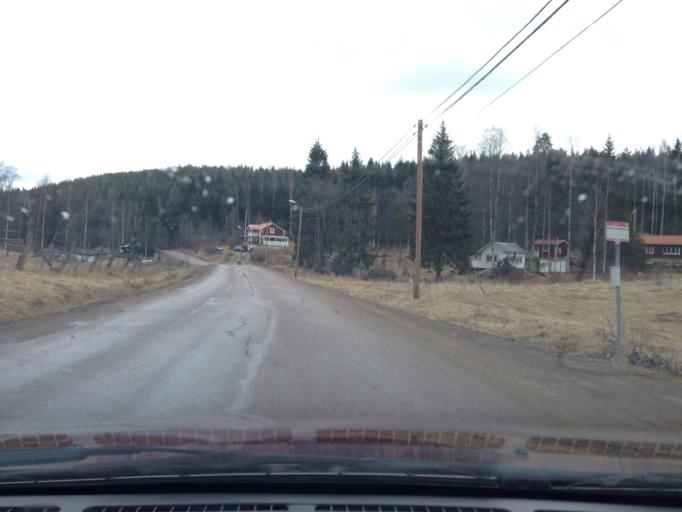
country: SE
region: Dalarna
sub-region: Ludvika Kommun
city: Ludvika
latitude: 60.1551
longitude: 15.2632
